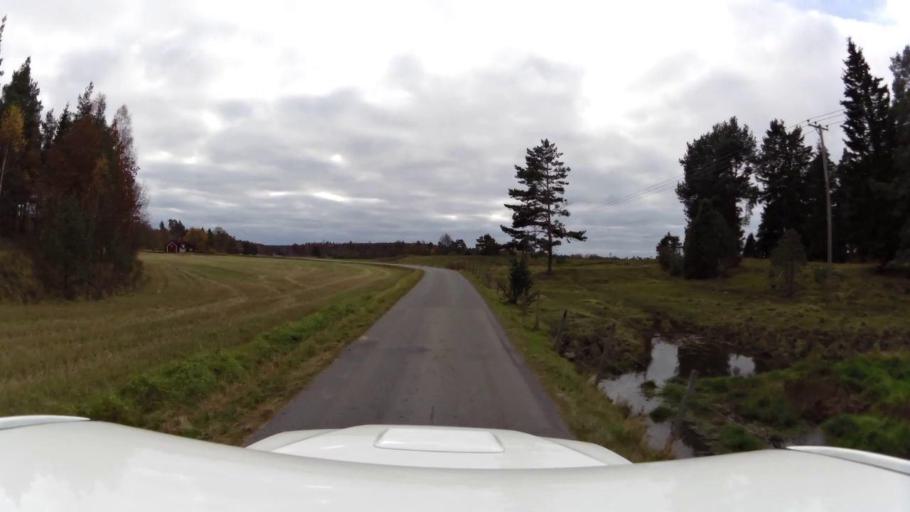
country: SE
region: OEstergoetland
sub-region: Linkopings Kommun
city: Linghem
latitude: 58.3902
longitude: 15.8356
